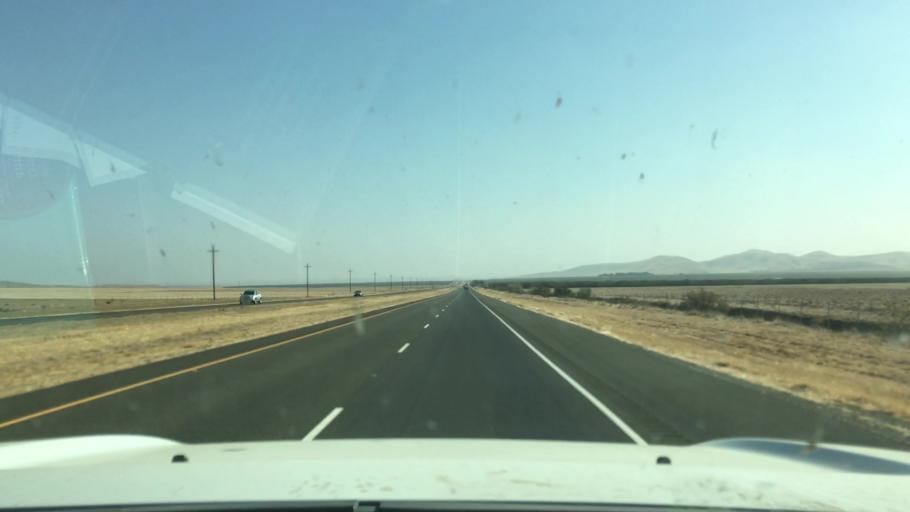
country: US
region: California
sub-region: San Luis Obispo County
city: Shandon
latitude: 35.6903
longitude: -120.1230
